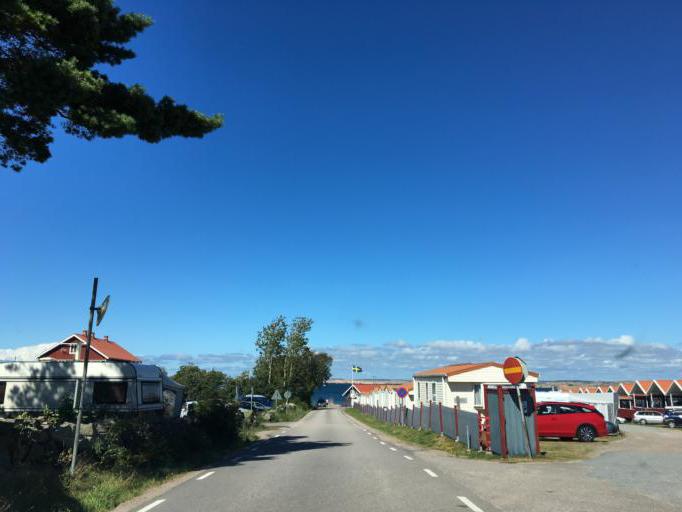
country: SE
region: Vaestra Goetaland
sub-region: Sotenas Kommun
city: Hunnebostrand
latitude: 58.4381
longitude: 11.2670
